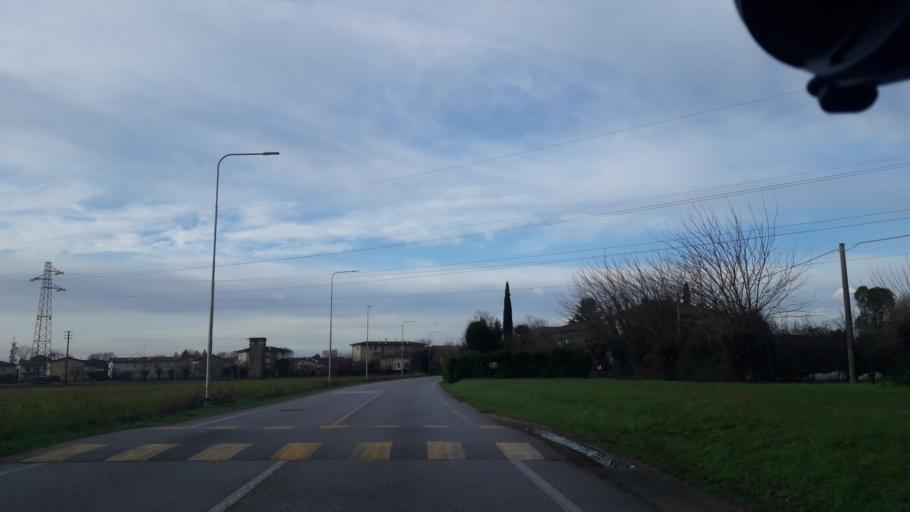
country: IT
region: Friuli Venezia Giulia
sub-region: Provincia di Udine
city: Udine
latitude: 46.0582
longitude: 13.2613
